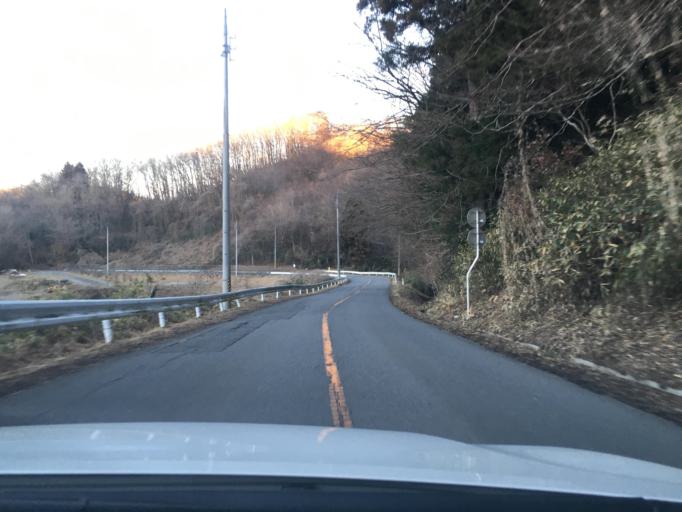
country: JP
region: Fukushima
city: Miharu
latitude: 37.4528
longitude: 140.5065
